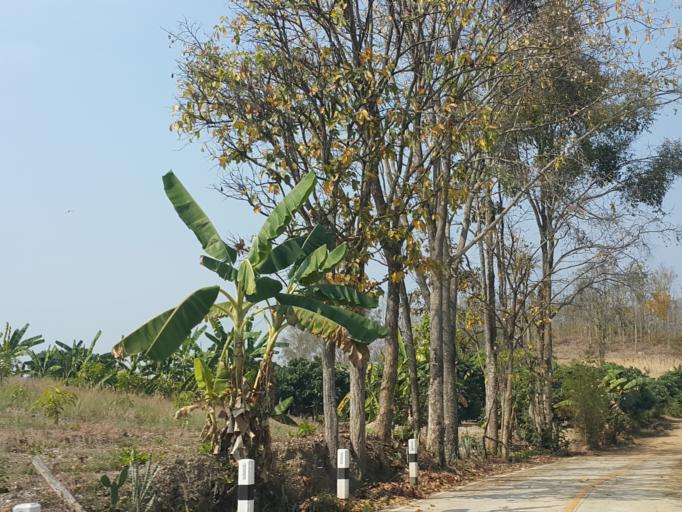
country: TH
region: Chiang Mai
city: Hang Dong
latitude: 18.7304
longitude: 98.8599
